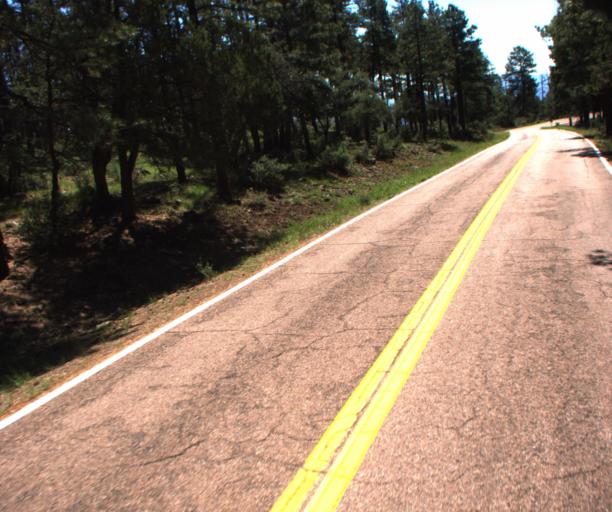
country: US
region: Arizona
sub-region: Greenlee County
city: Morenci
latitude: 33.5225
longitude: -109.3073
